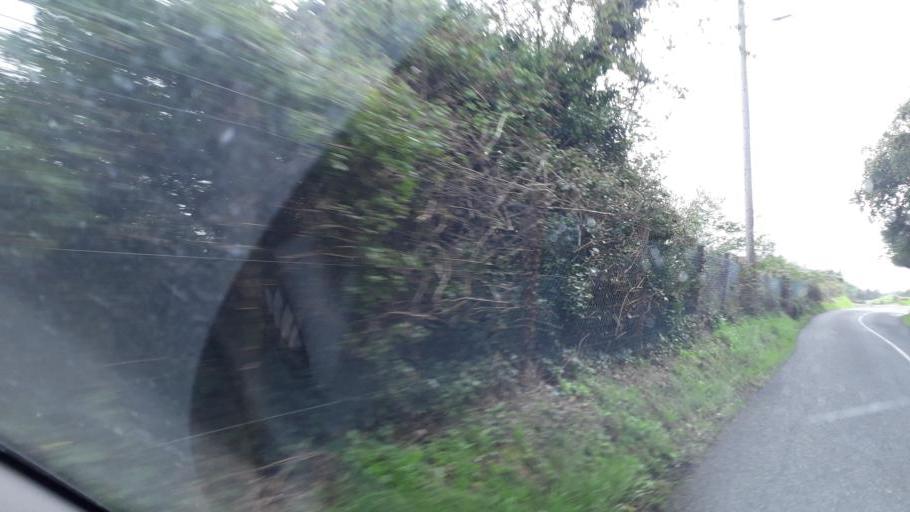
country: IE
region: Leinster
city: Sandyford
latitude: 53.2543
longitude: -6.2198
